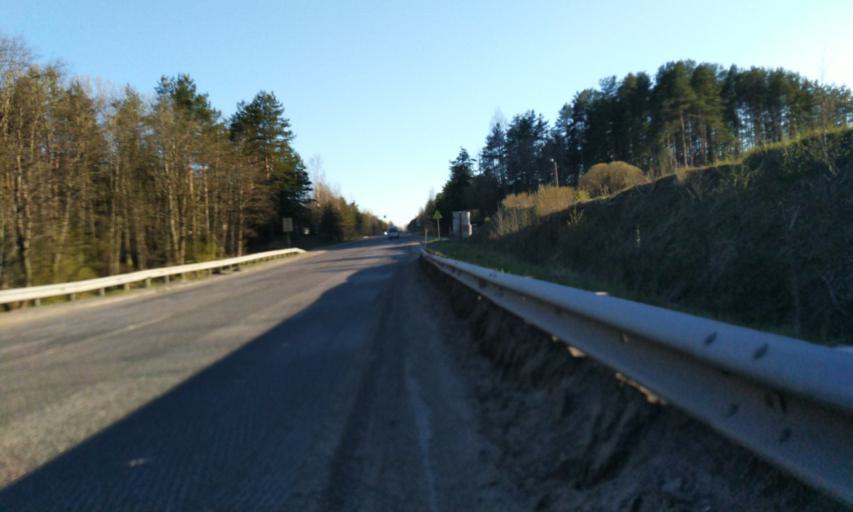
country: RU
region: Leningrad
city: Toksovo
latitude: 60.1297
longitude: 30.5203
